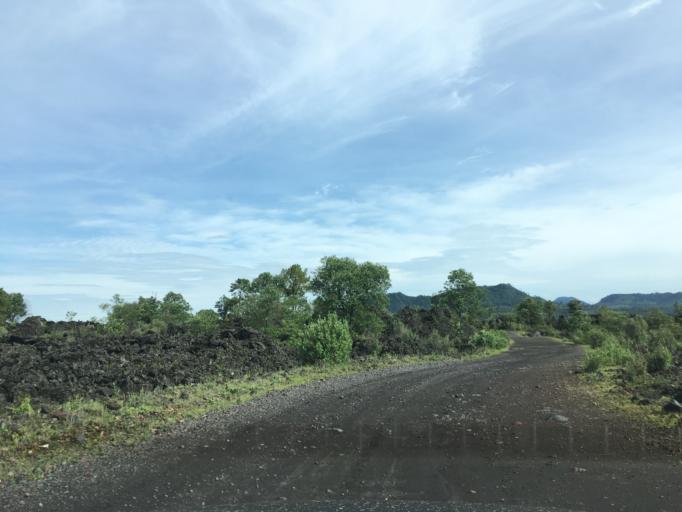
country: MX
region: Michoacan
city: Angahuan
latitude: 19.5280
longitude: -102.2492
